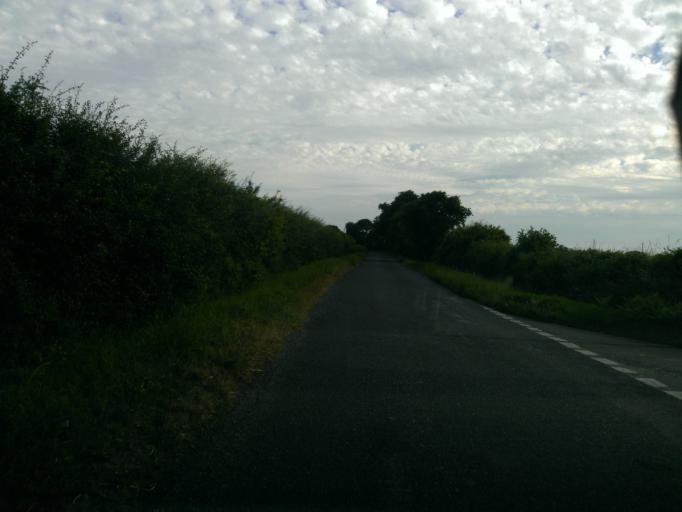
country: GB
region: England
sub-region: Essex
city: Great Bentley
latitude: 51.8392
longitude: 1.0849
